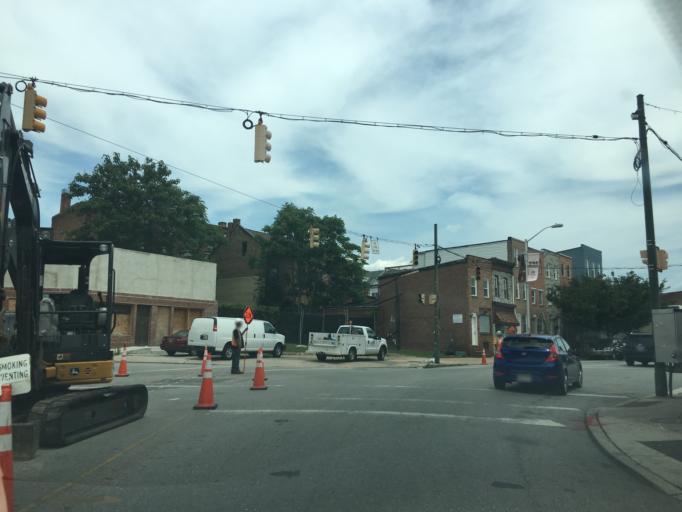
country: US
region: Maryland
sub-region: City of Baltimore
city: Baltimore
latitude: 39.2827
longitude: -76.6328
